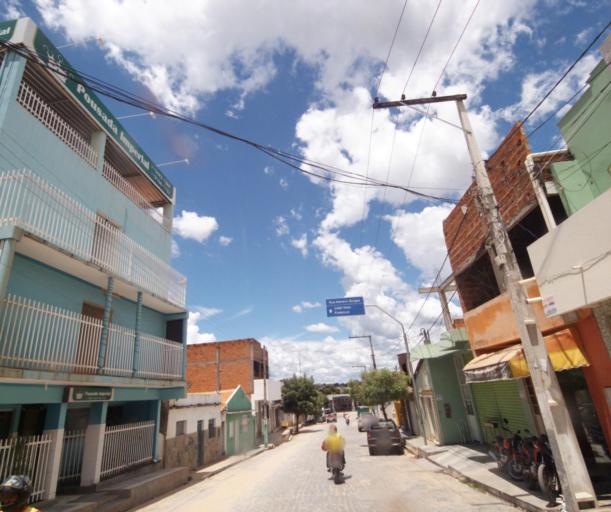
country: BR
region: Bahia
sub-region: Sao Felix Do Coribe
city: Santa Maria da Vitoria
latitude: -13.3983
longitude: -44.2029
